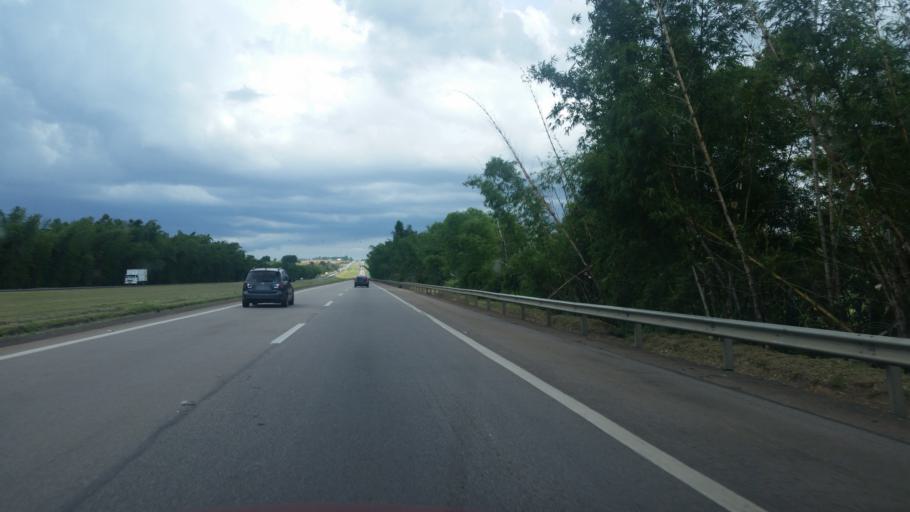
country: BR
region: Sao Paulo
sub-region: Boituva
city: Boituva
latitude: -23.2869
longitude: -47.7657
